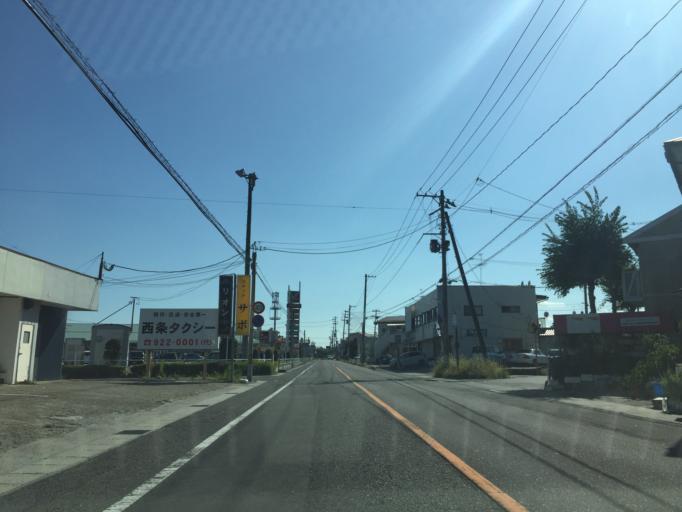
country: JP
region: Fukushima
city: Koriyama
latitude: 37.4033
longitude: 140.3275
